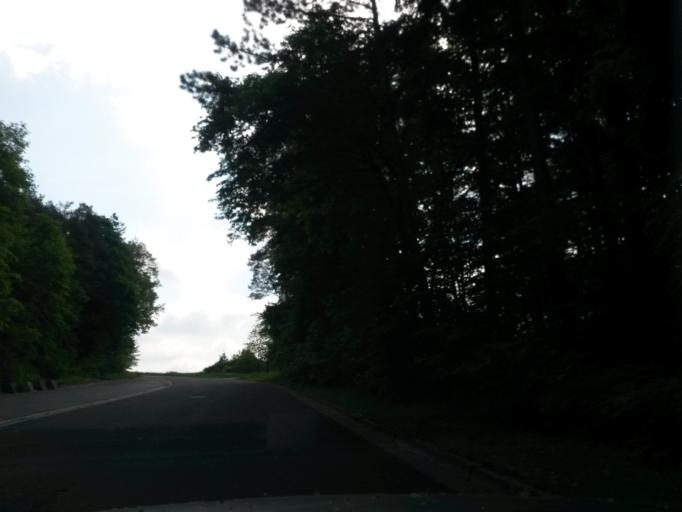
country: DE
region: Bavaria
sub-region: Regierungsbezirk Unterfranken
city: Bad Kissingen
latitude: 50.1969
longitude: 10.0938
